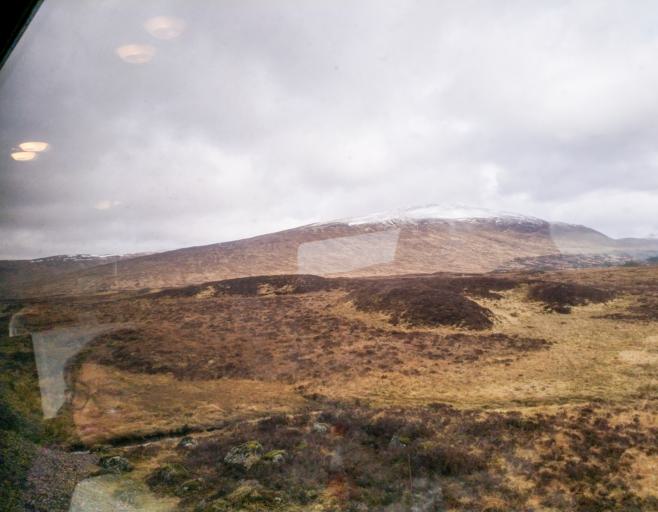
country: GB
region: Scotland
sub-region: Highland
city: Spean Bridge
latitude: 56.7546
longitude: -4.6843
